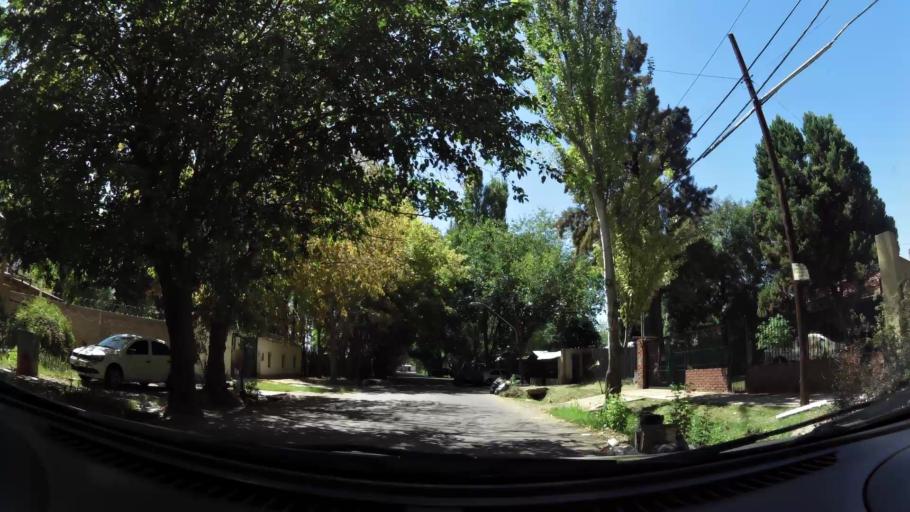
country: AR
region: Mendoza
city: Las Heras
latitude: -32.8662
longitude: -68.7985
